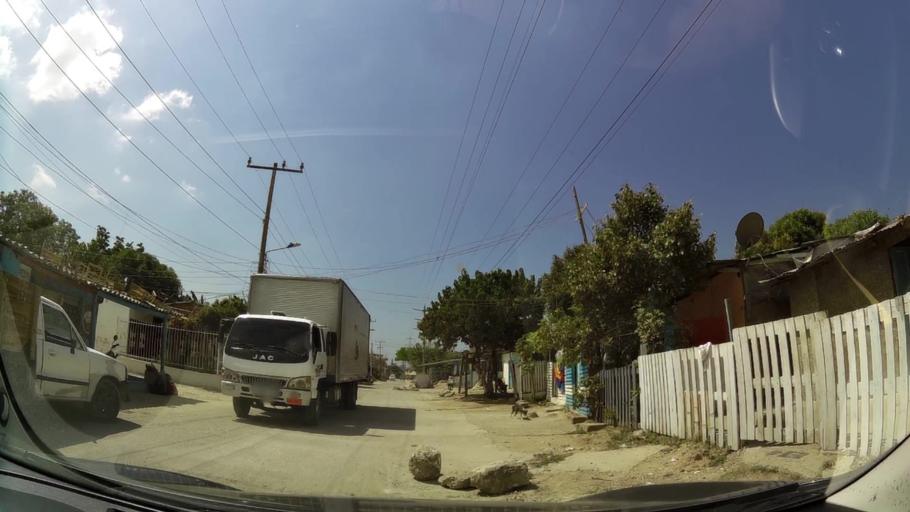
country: CO
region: Bolivar
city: Cartagena
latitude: 10.3467
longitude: -75.4913
